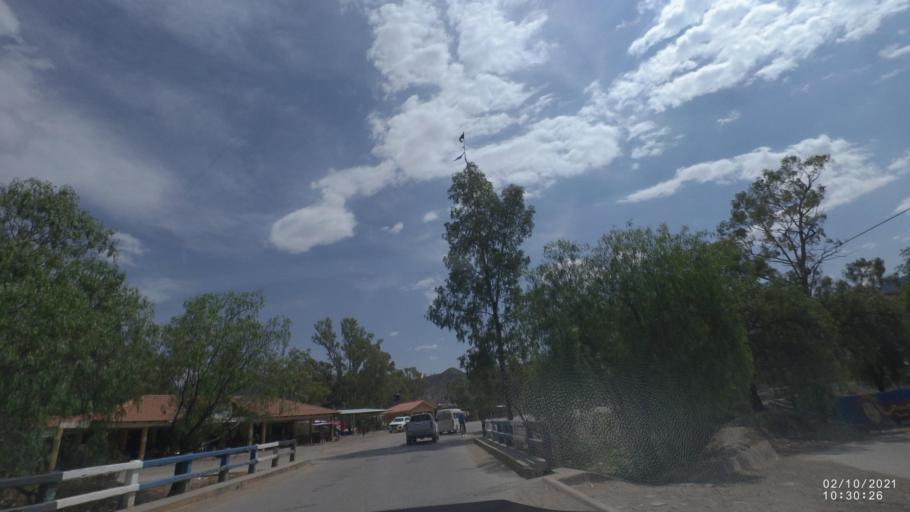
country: BO
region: Cochabamba
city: Capinota
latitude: -17.6971
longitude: -66.2653
